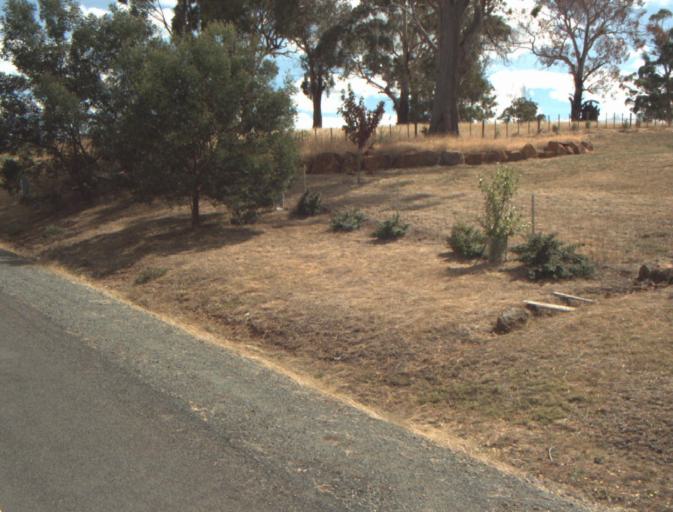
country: AU
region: Tasmania
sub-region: Launceston
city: Mayfield
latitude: -41.3460
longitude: 147.0874
